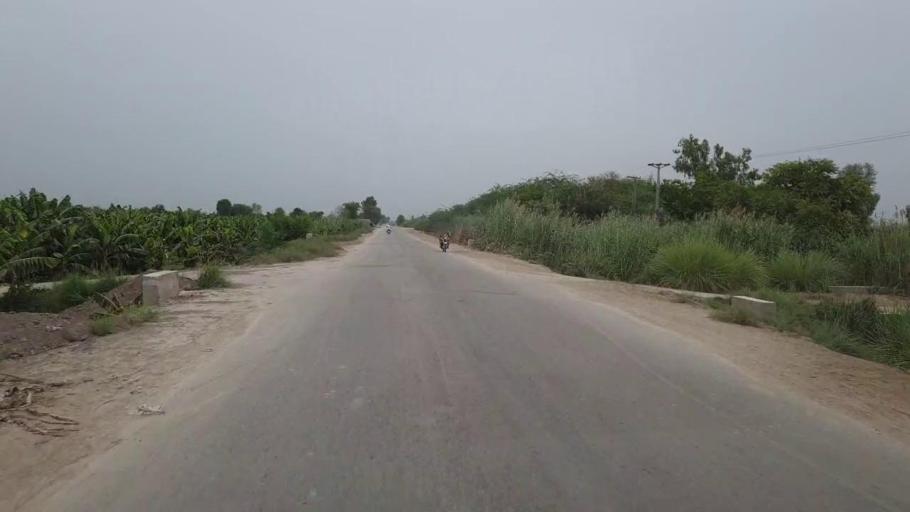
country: PK
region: Sindh
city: Bandhi
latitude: 26.5505
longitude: 68.2142
